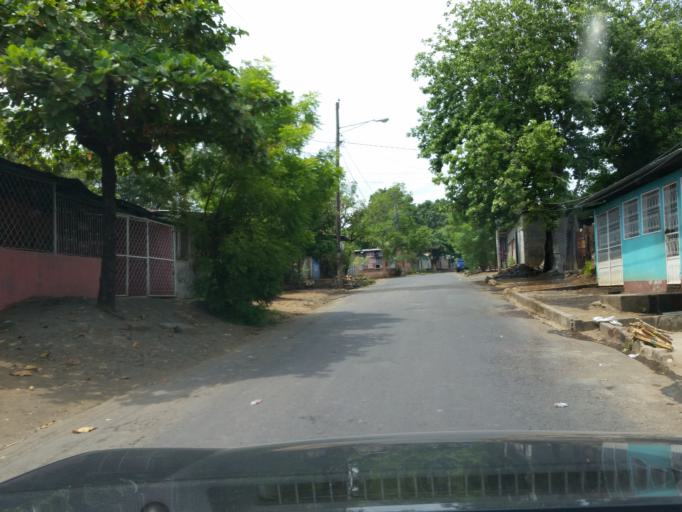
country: NI
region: Managua
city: Managua
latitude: 12.1204
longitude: -86.2721
